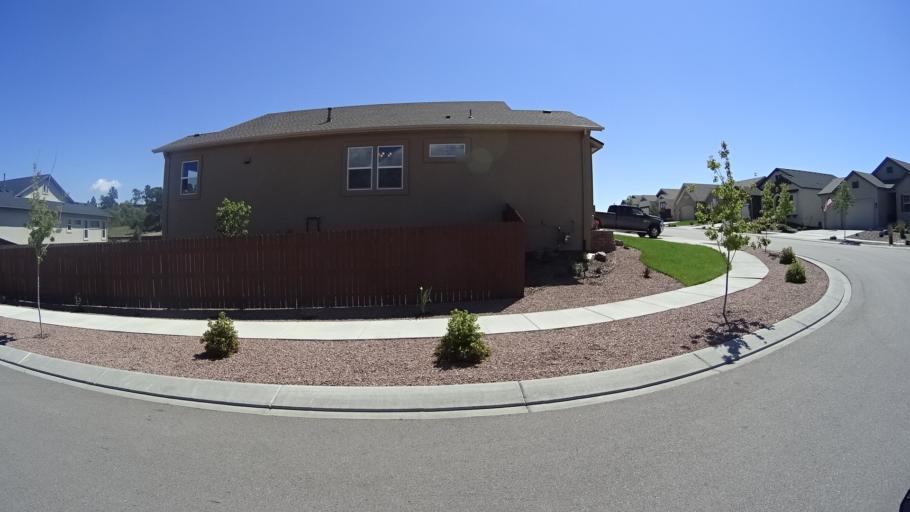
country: US
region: Colorado
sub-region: El Paso County
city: Black Forest
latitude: 38.9932
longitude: -104.7619
